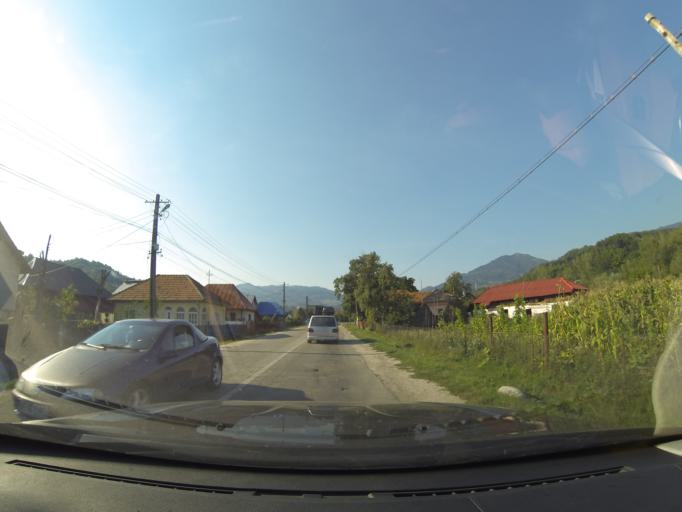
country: RO
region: Arges
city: Poenari
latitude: 45.3153
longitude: 24.6440
